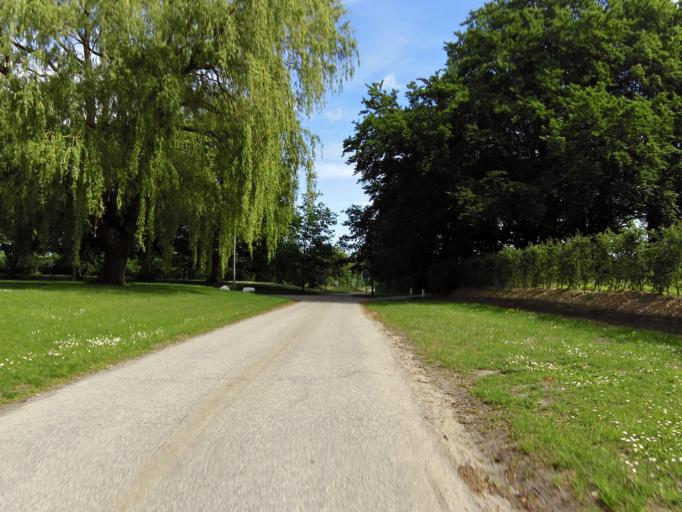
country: SE
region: Skane
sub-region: Staffanstorps Kommun
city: Hjaerup
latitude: 55.7008
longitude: 13.1427
